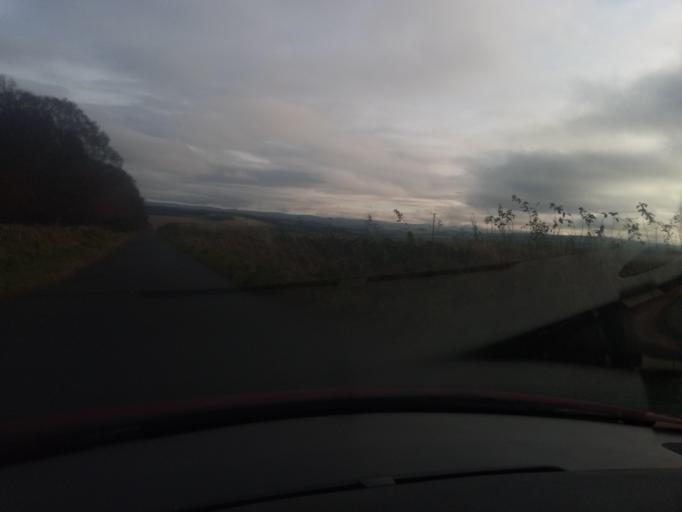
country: GB
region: Scotland
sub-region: The Scottish Borders
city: Jedburgh
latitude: 55.4804
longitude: -2.5724
